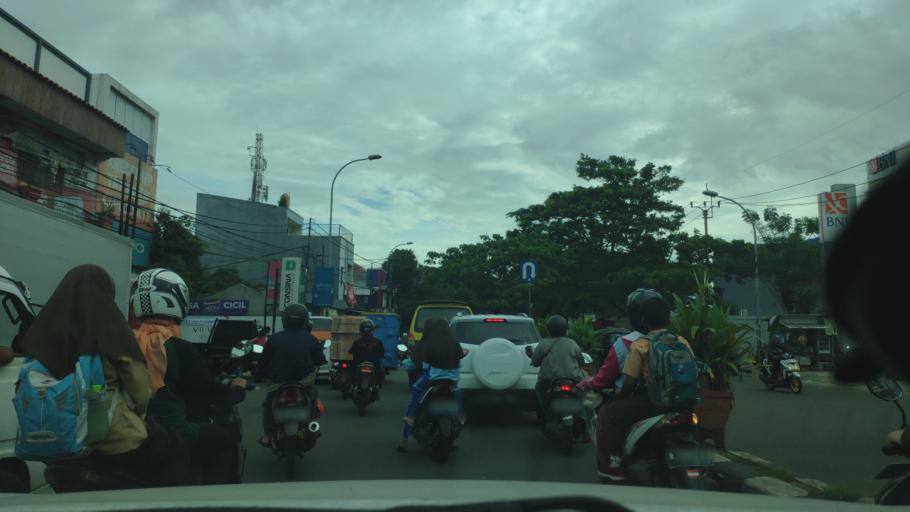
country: ID
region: West Java
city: Ciputat
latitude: -6.2263
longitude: 106.7051
